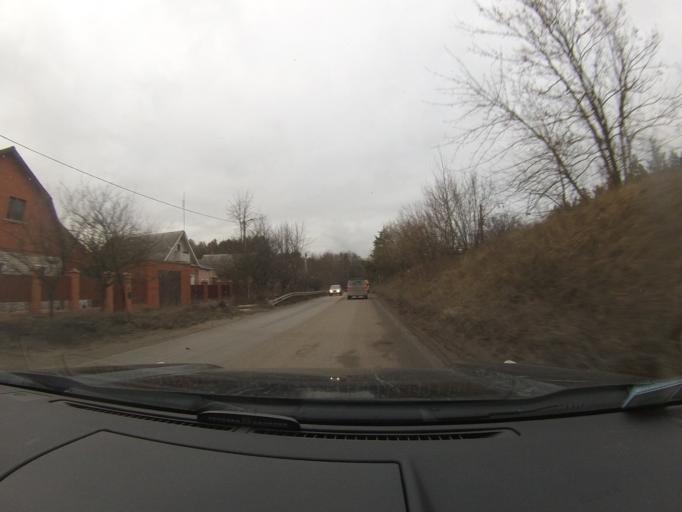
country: RU
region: Moskovskaya
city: Voskresensk
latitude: 55.3315
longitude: 38.6784
